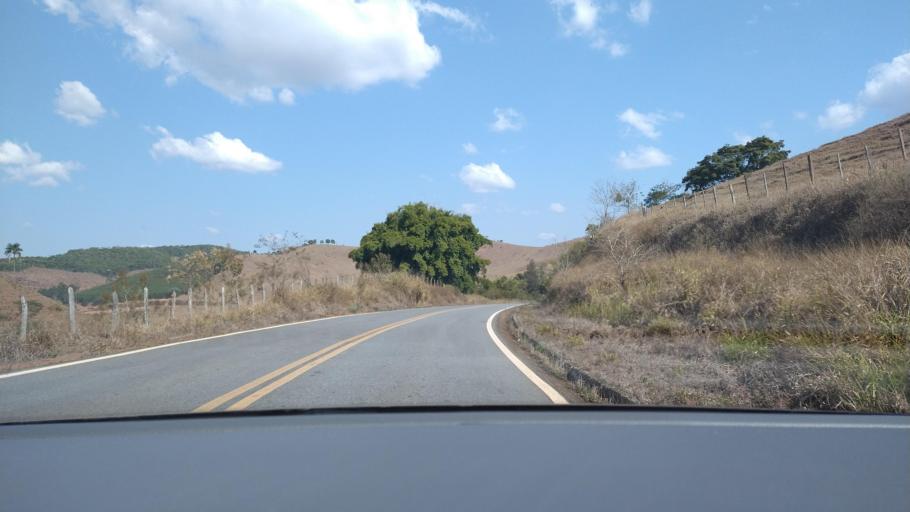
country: BR
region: Minas Gerais
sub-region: Rio Piracicaba
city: Rio Piracicaba
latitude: -19.9606
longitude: -43.1562
